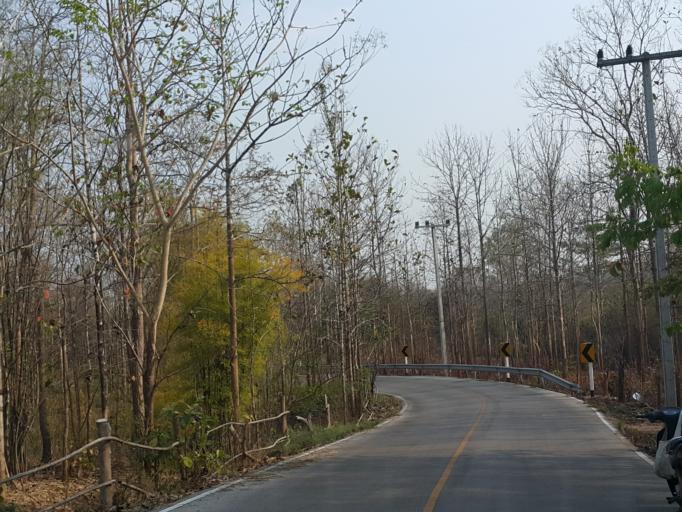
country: TH
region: Lampang
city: Chae Hom
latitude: 18.7285
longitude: 99.5460
